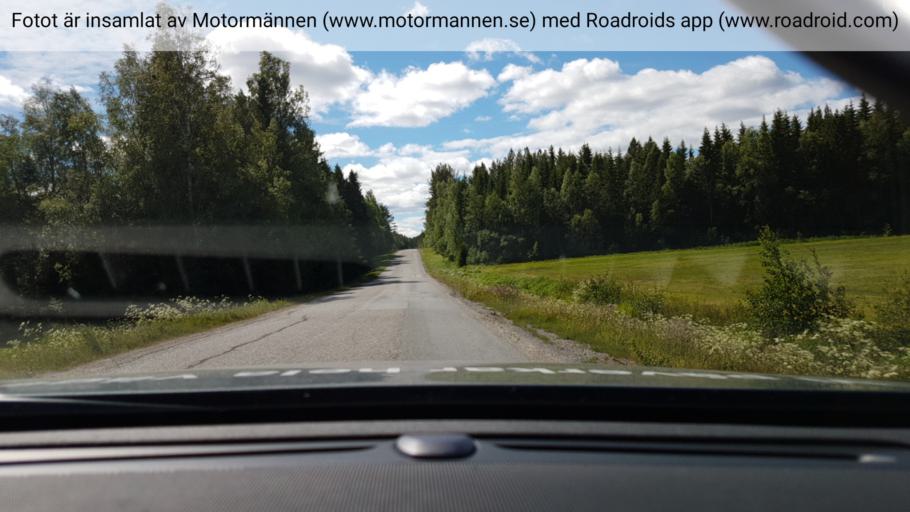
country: SE
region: Vaesterbotten
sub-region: Skelleftea Kommun
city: Burea
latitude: 64.4099
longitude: 21.3496
